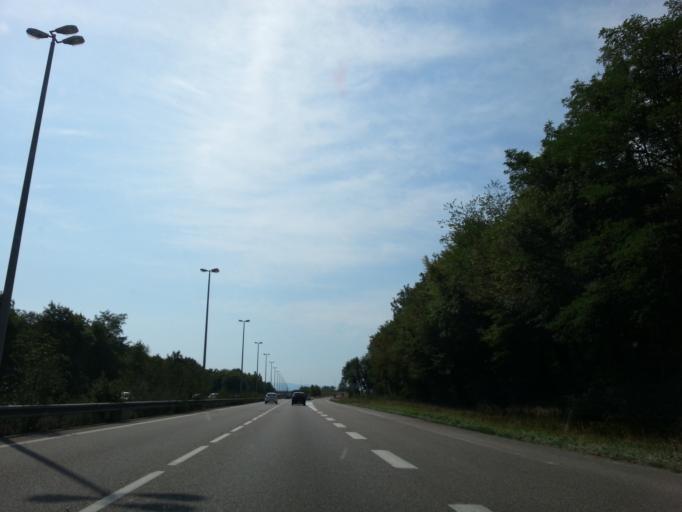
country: FR
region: Alsace
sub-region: Departement du Haut-Rhin
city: Bartenheim
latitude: 47.6413
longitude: 7.4974
